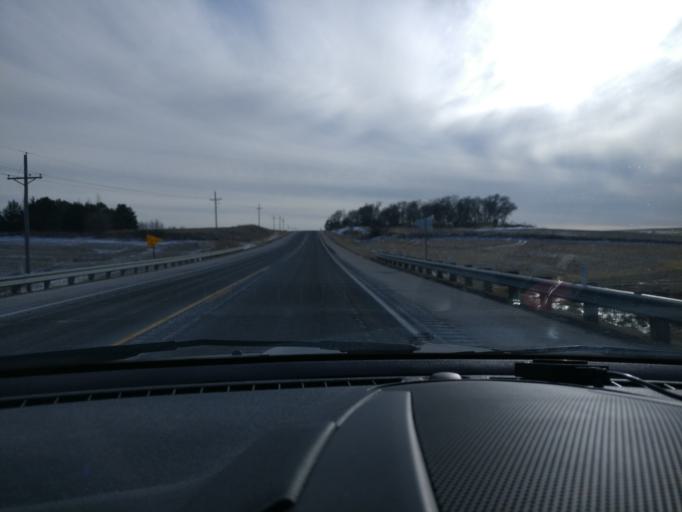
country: US
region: Nebraska
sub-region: Dodge County
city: Fremont
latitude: 41.3297
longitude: -96.5024
